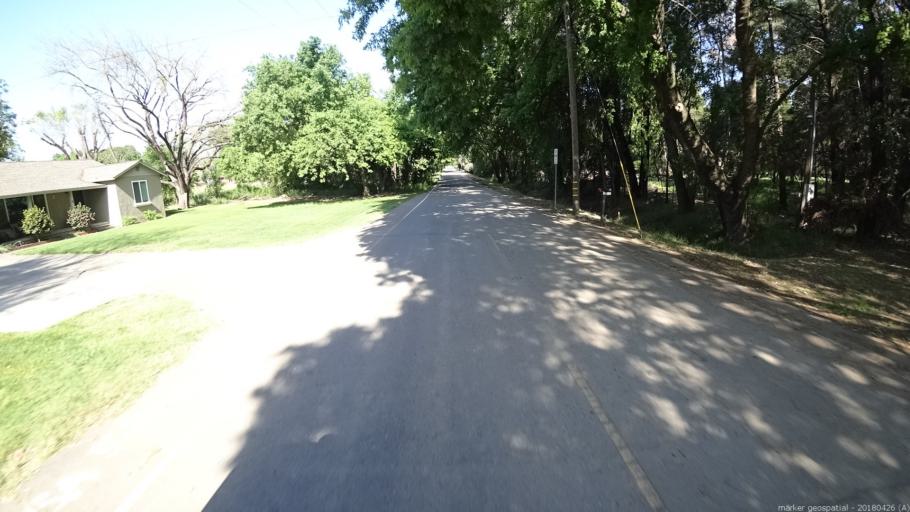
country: US
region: California
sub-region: Yolo County
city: West Sacramento
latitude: 38.5415
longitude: -121.5165
